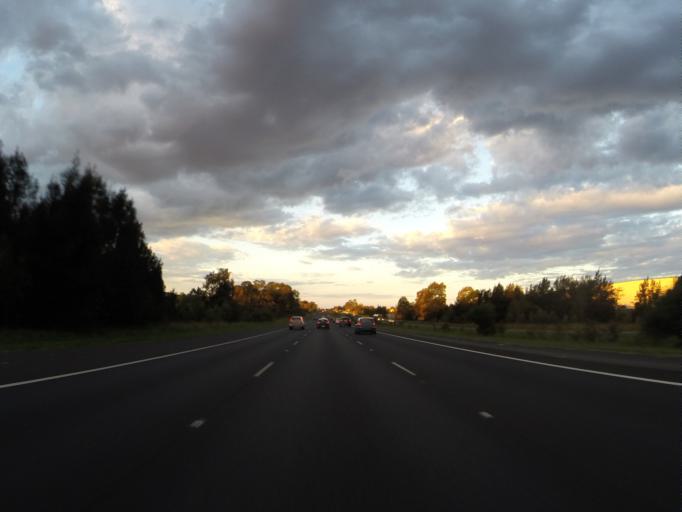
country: AU
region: New South Wales
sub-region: Campbelltown Municipality
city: Campbelltown
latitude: -34.0558
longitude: 150.7993
